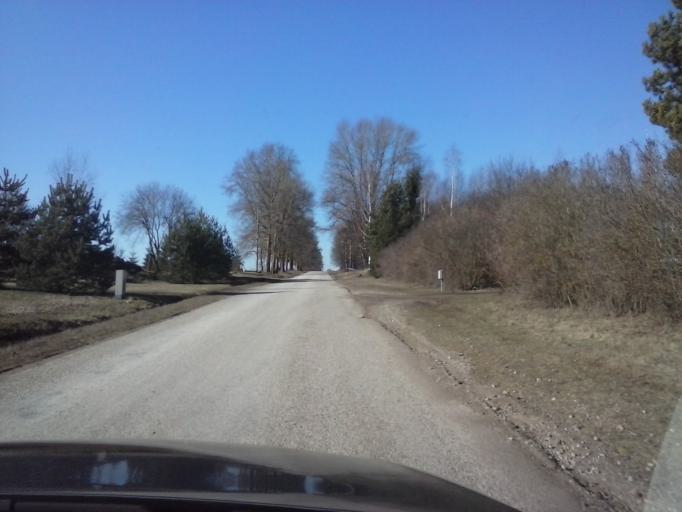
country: EE
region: Tartu
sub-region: Noo vald
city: Noo
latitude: 58.3072
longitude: 26.5925
